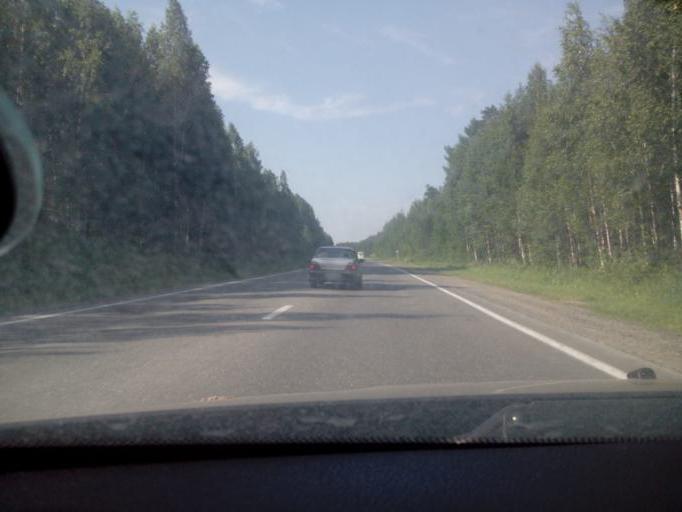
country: RU
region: Sverdlovsk
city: Verkh-Neyvinskiy
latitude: 57.2710
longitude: 60.2947
